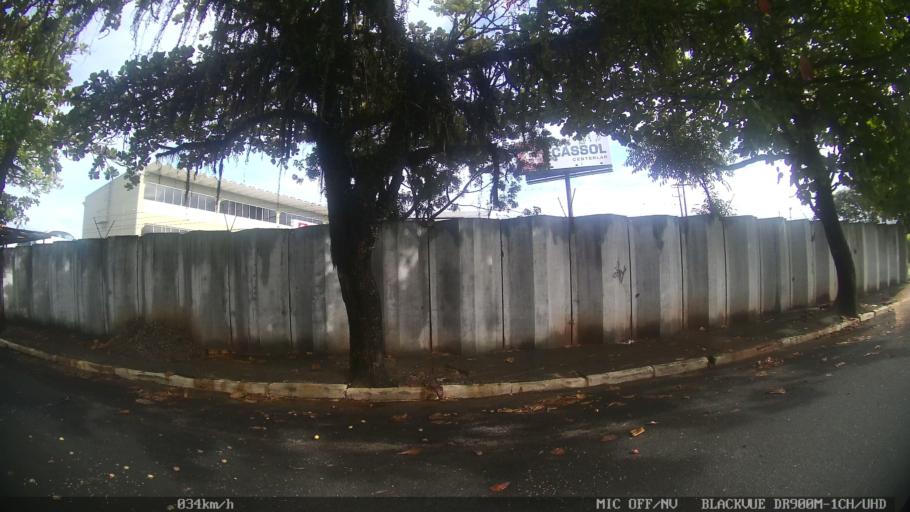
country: BR
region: Santa Catarina
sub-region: Sao Jose
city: Campinas
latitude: -27.5885
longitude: -48.6137
